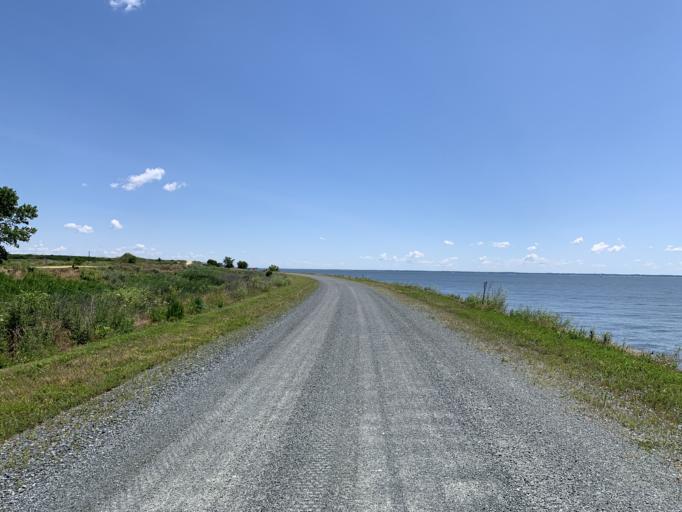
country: US
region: Maryland
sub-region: Baltimore County
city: Edgemere
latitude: 39.2381
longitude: -76.3720
